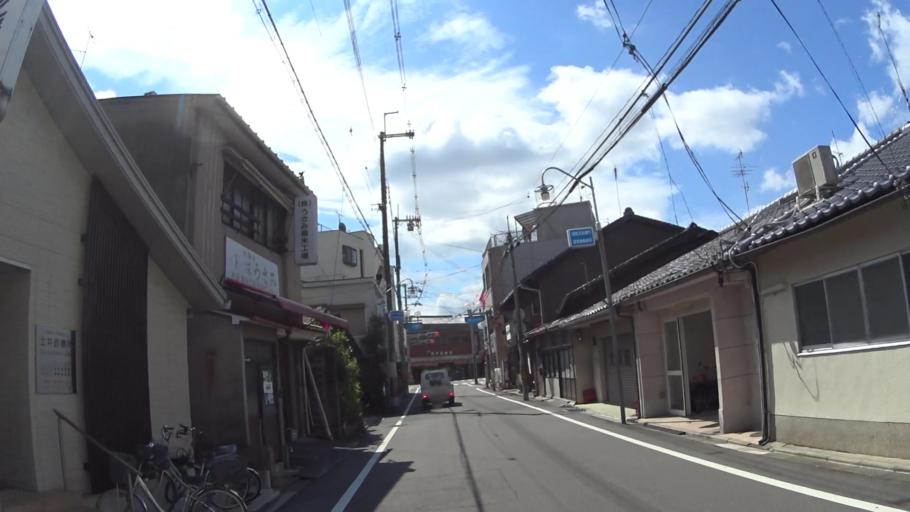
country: JP
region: Kyoto
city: Muko
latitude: 34.9898
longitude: 135.7184
